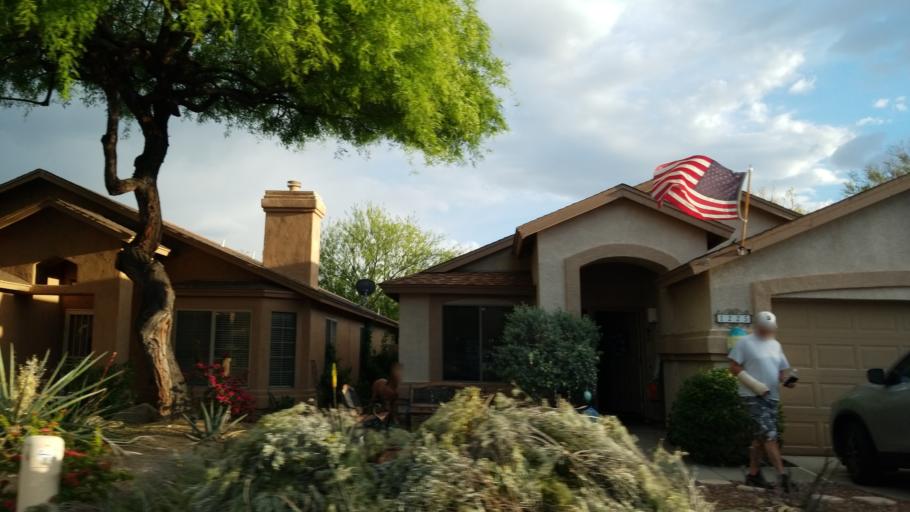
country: US
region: Arizona
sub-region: Maricopa County
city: Paradise Valley
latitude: 33.5895
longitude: -112.0554
